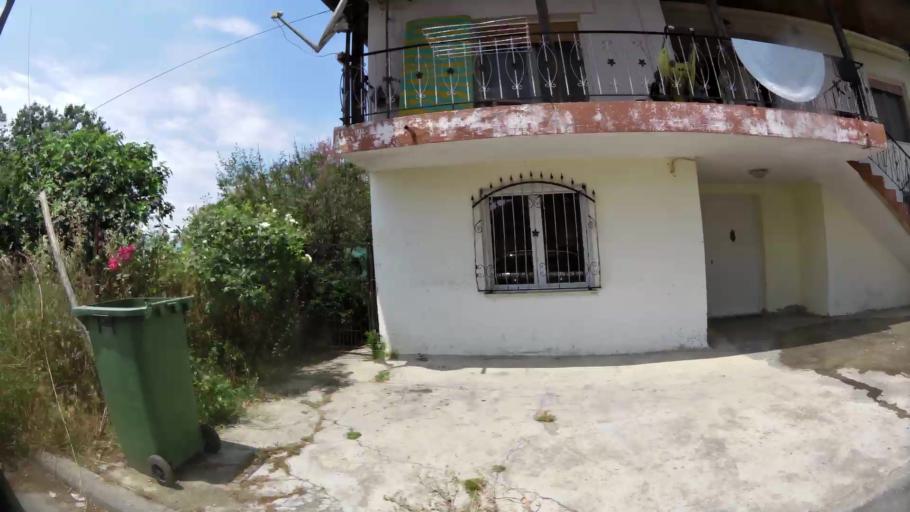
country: GR
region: Central Macedonia
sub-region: Nomos Pierias
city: Peristasi
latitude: 40.2765
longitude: 22.5396
